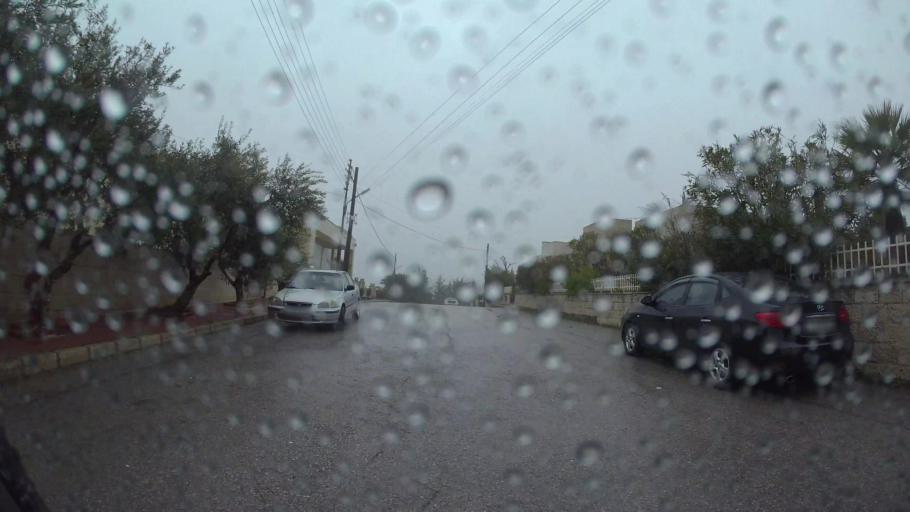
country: JO
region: Amman
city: Al Jubayhah
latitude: 32.0006
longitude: 35.8233
